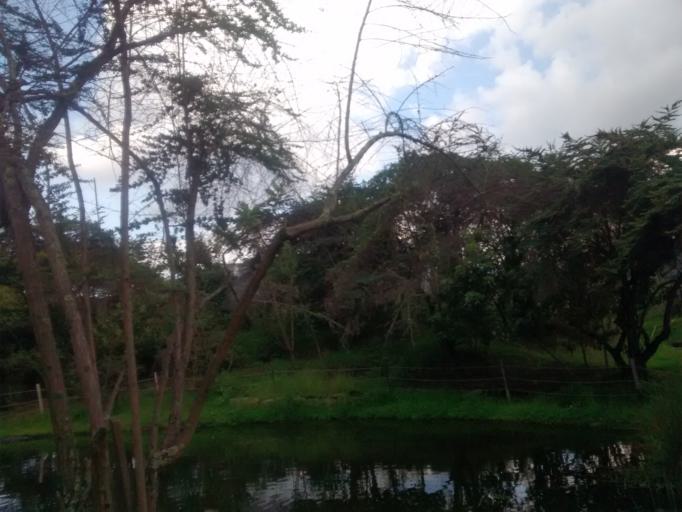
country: CO
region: Bogota D.C.
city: Bogota
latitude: 4.6670
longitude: -74.0999
